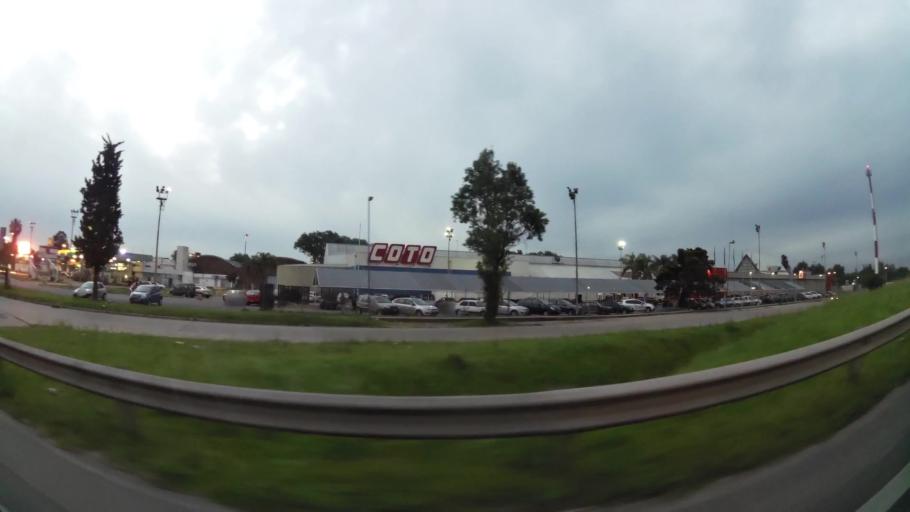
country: AR
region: Santa Fe
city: Granadero Baigorria
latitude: -32.9300
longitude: -60.7237
